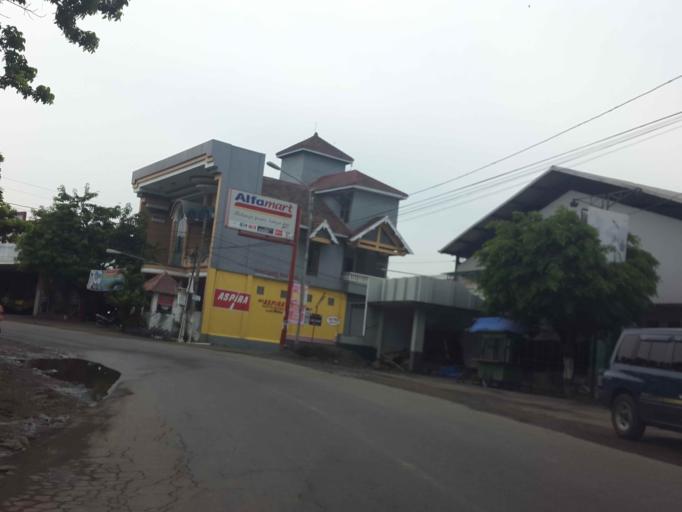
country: ID
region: Central Java
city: Mranggen
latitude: -6.9782
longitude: 110.4805
